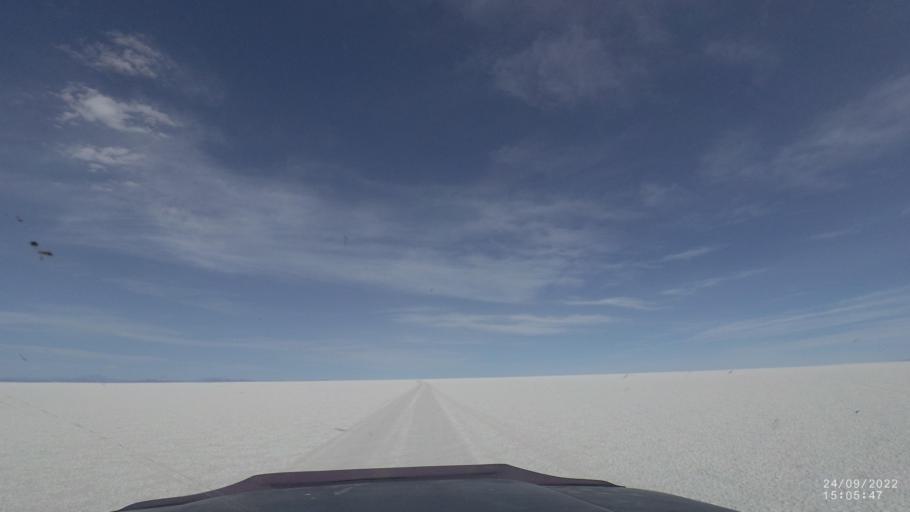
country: BO
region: Potosi
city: Colchani
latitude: -19.9088
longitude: -67.5147
